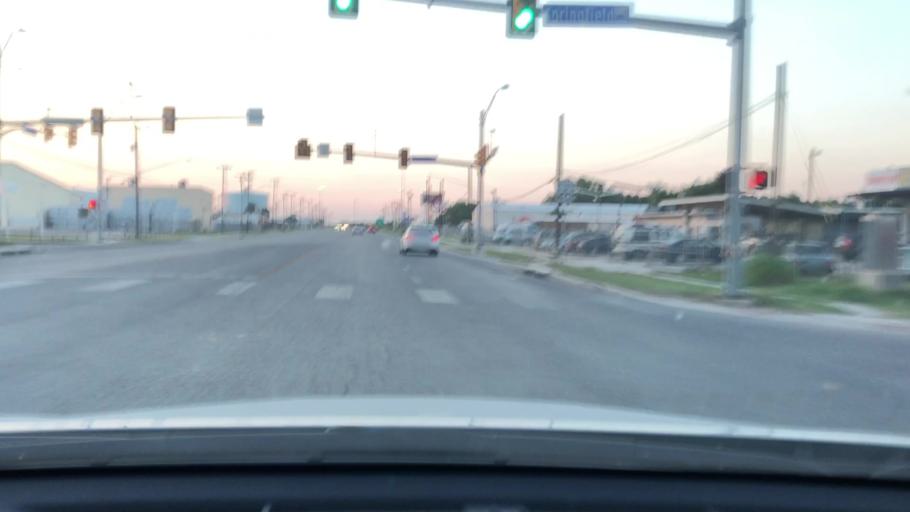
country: US
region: Texas
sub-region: Bexar County
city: Kirby
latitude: 29.4407
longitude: -98.4051
